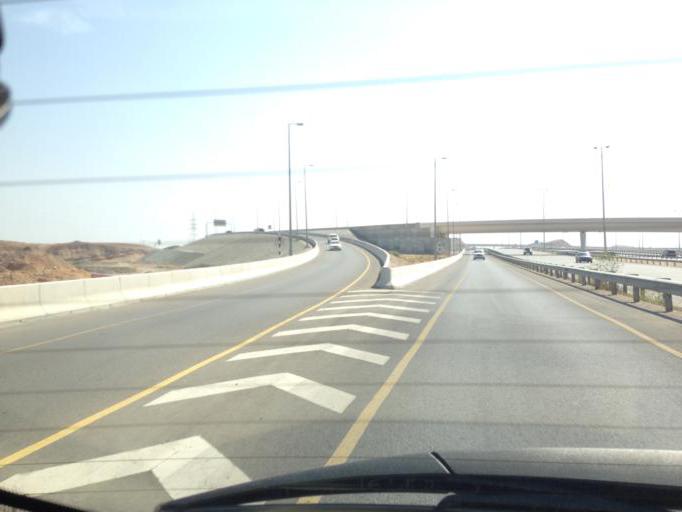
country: OM
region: Muhafazat Masqat
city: As Sib al Jadidah
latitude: 23.5677
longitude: 58.1849
